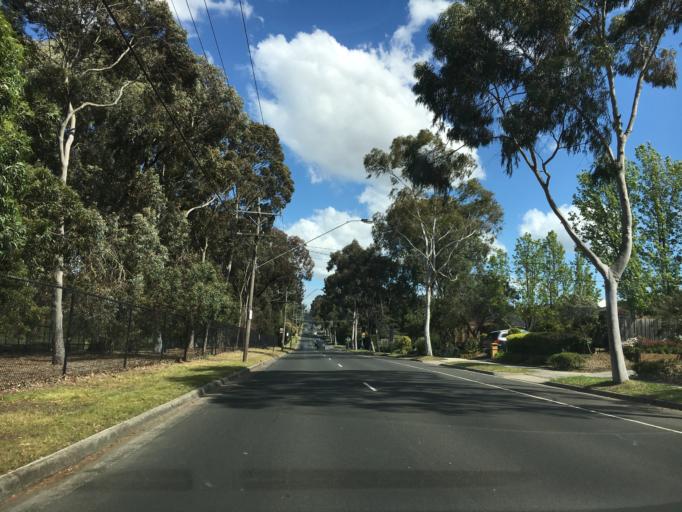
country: AU
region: Victoria
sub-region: Monash
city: Mulgrave
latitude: -37.8927
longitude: 145.1917
